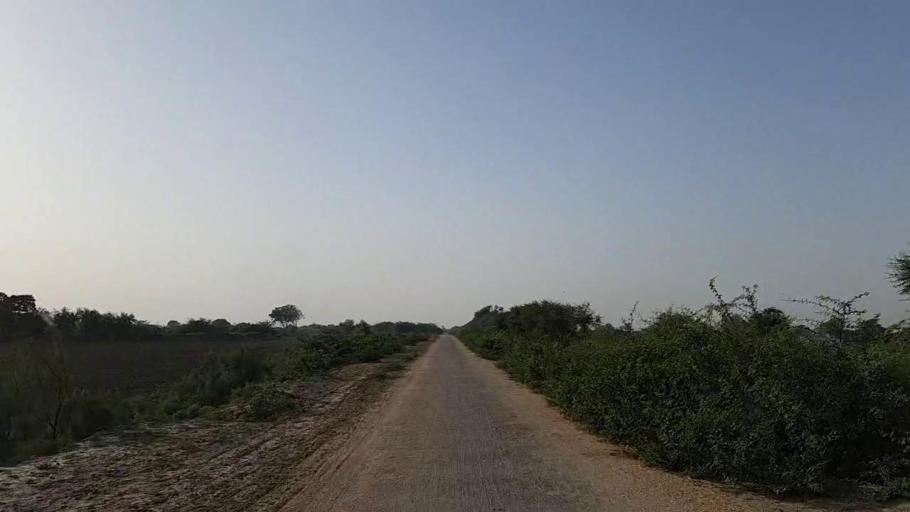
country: PK
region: Sindh
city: Jati
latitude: 24.3349
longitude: 68.1544
